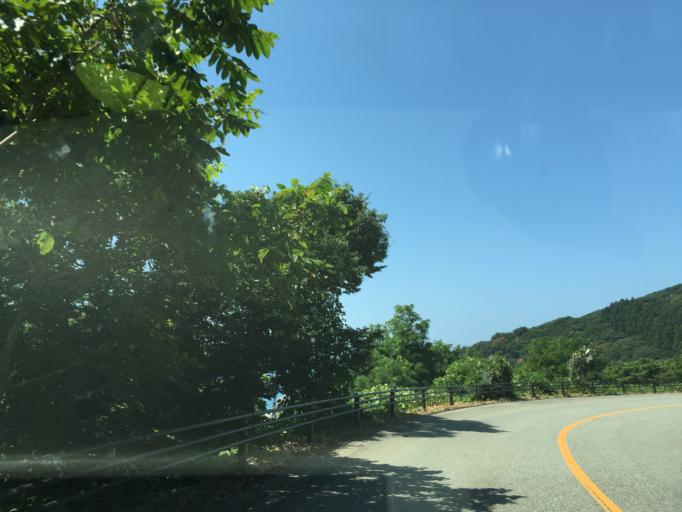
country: JP
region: Akita
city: Tenno
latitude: 39.9112
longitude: 139.7310
